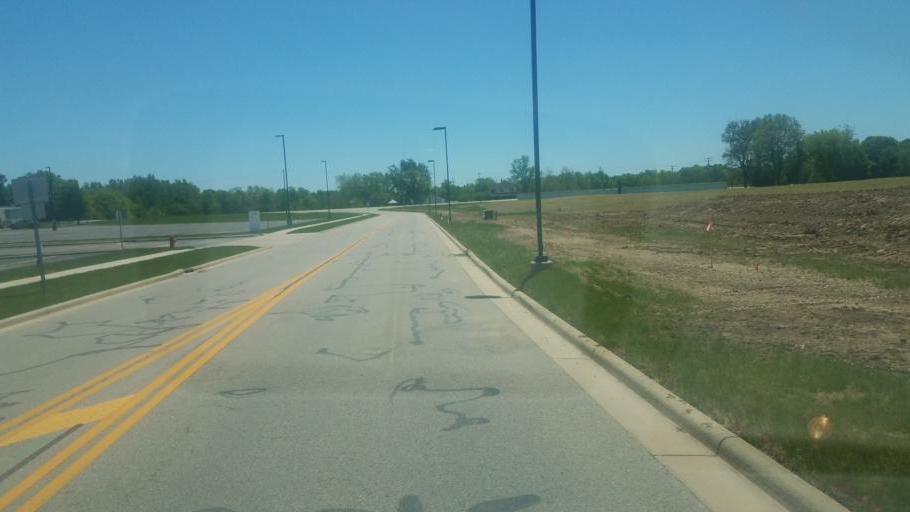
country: US
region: Ohio
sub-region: Darke County
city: Versailles
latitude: 40.2277
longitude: -84.4938
